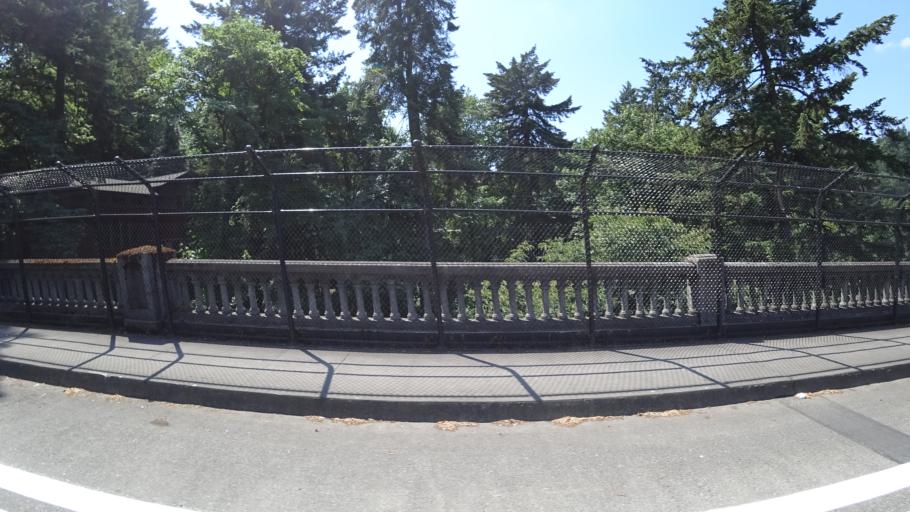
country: US
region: Oregon
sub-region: Multnomah County
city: Portland
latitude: 45.5190
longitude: -122.6975
